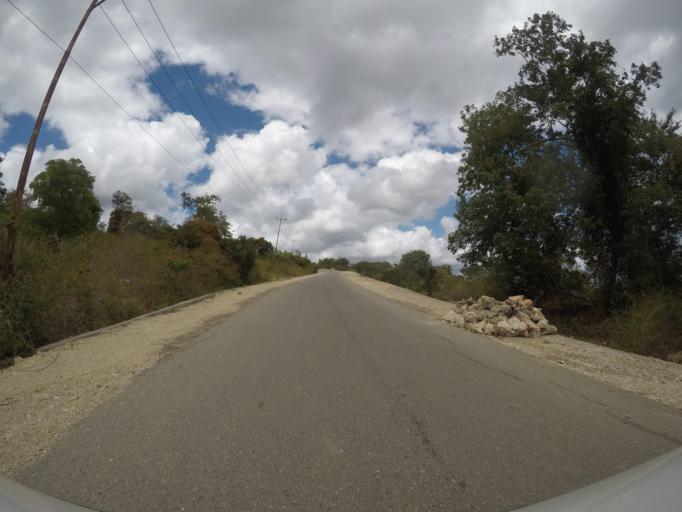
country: TL
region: Lautem
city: Lospalos
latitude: -8.3677
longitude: 126.9278
